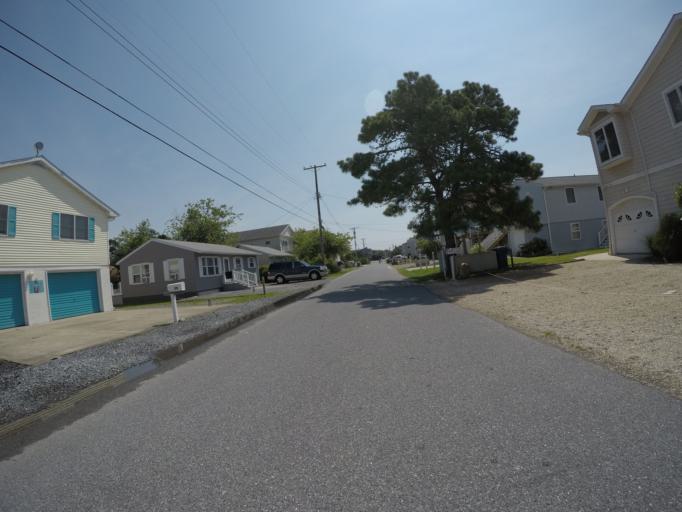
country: US
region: Delaware
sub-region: Sussex County
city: Bethany Beach
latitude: 38.5185
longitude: -75.0572
